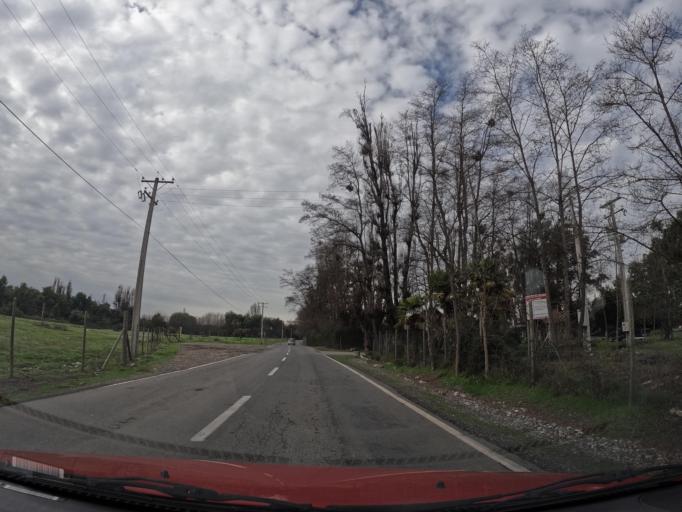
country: CL
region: Maule
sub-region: Provincia de Linares
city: Linares
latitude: -35.8666
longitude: -71.6285
